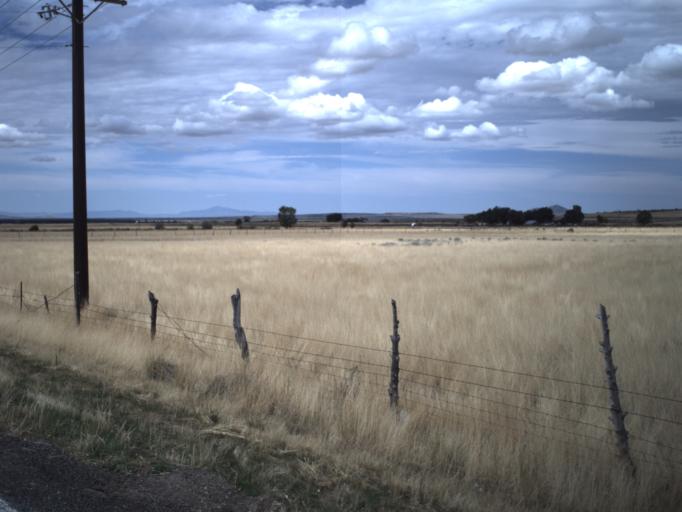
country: US
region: Utah
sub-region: Millard County
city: Fillmore
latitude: 38.9792
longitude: -112.3931
